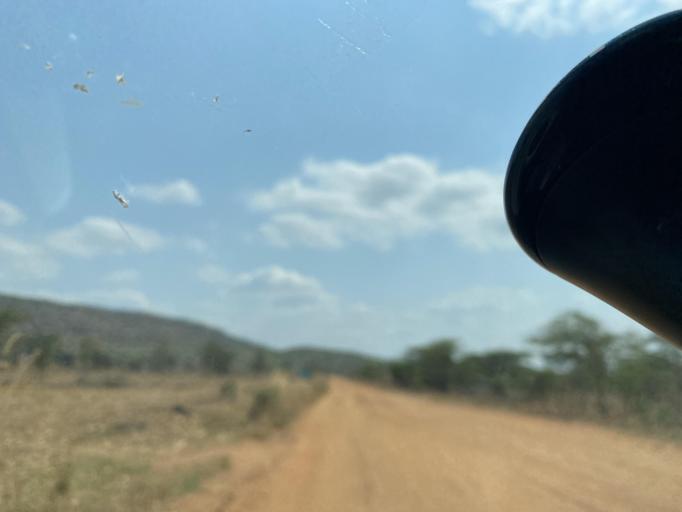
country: ZM
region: Lusaka
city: Chongwe
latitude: -15.6000
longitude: 28.7512
